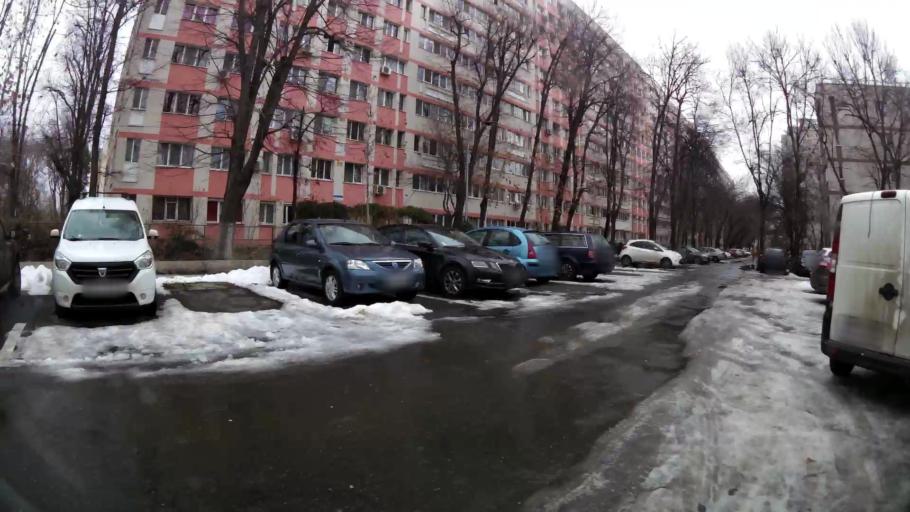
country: RO
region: Ilfov
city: Dobroesti
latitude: 44.4252
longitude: 26.1733
